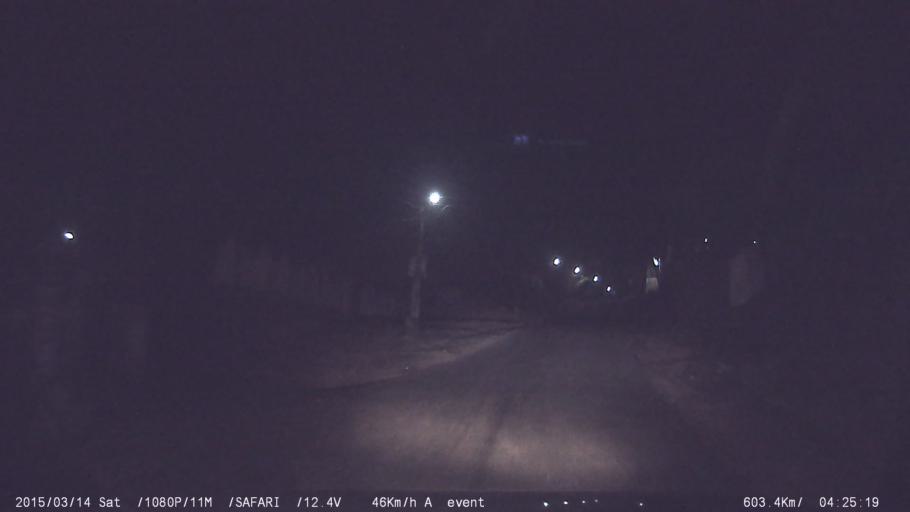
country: IN
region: Kerala
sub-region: Kottayam
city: Changanacheri
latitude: 9.4347
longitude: 76.5614
